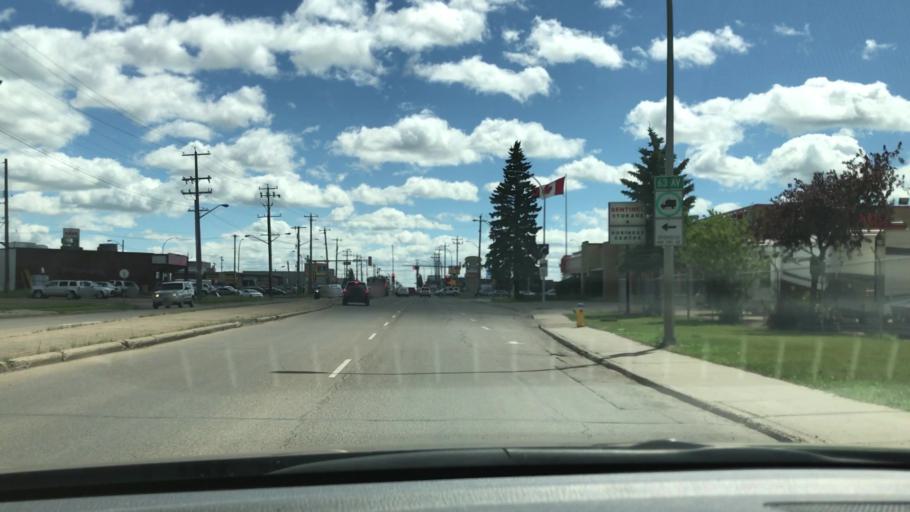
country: CA
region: Alberta
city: Edmonton
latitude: 53.5014
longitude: -113.4863
